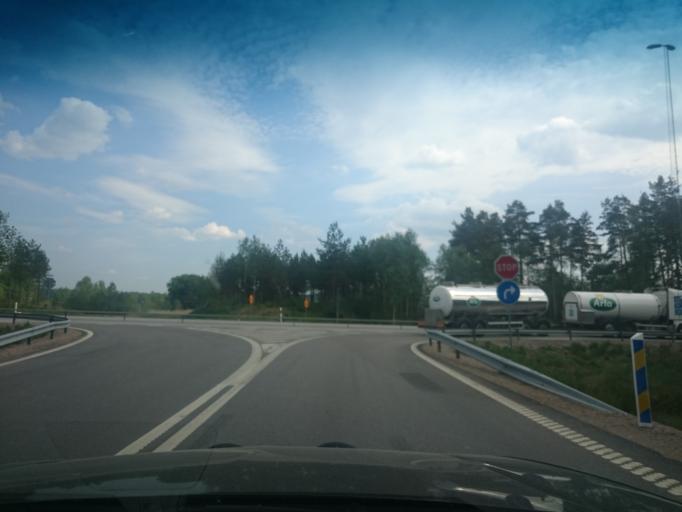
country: SE
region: Joenkoeping
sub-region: Vetlanda Kommun
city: Vetlanda
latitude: 57.4191
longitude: 15.1093
